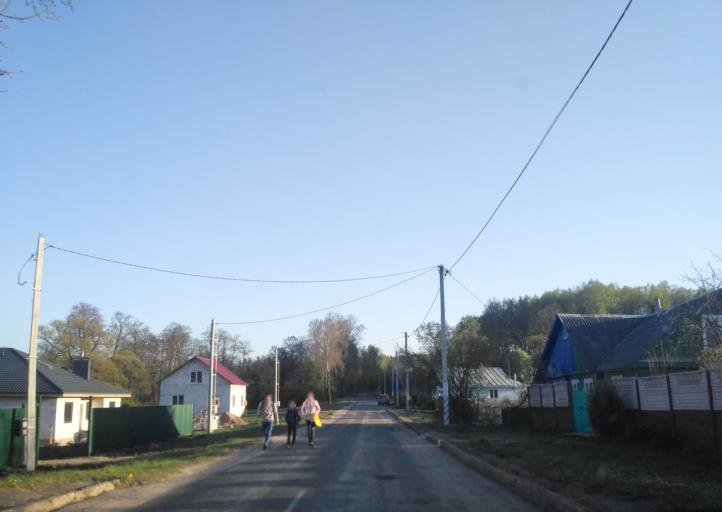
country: BY
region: Minsk
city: Pyatryshki
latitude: 54.0954
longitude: 27.1948
